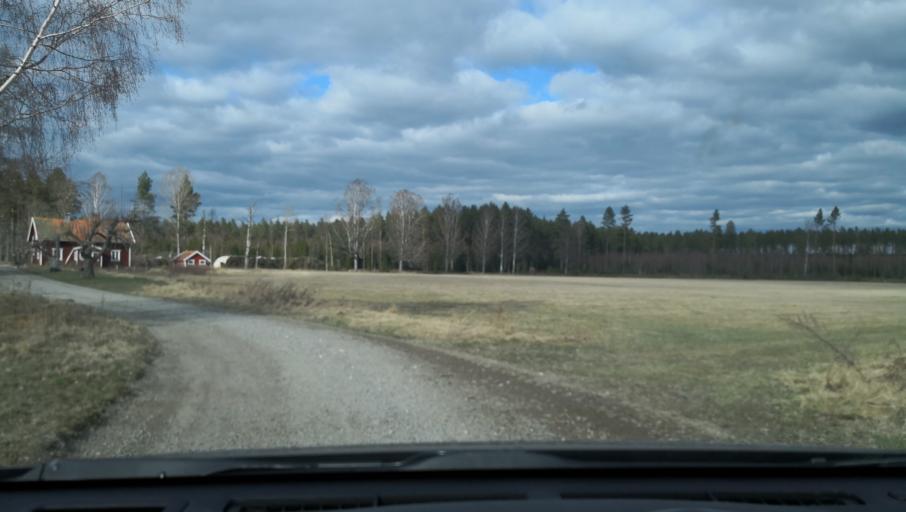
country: SE
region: Soedermanland
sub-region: Katrineholms Kommun
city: Katrineholm
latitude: 59.1256
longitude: 16.1450
